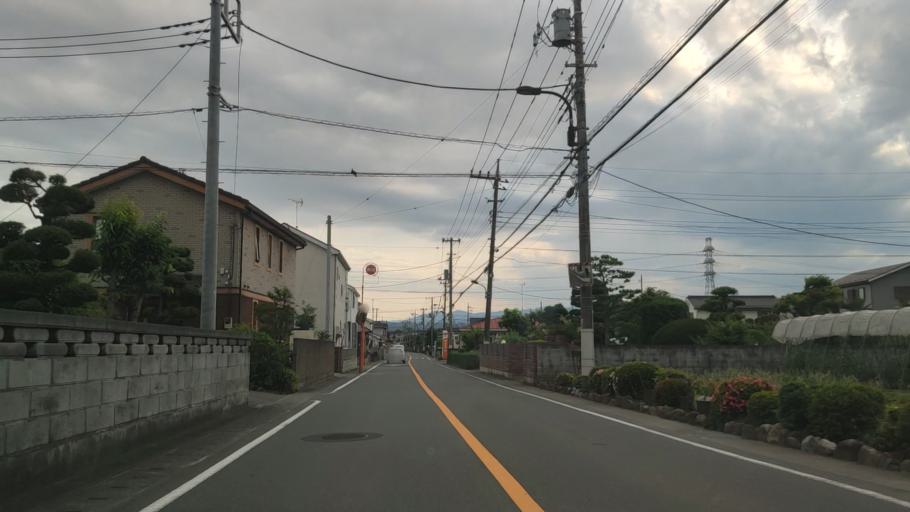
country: JP
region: Saitama
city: Hanno
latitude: 35.8030
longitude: 139.3041
